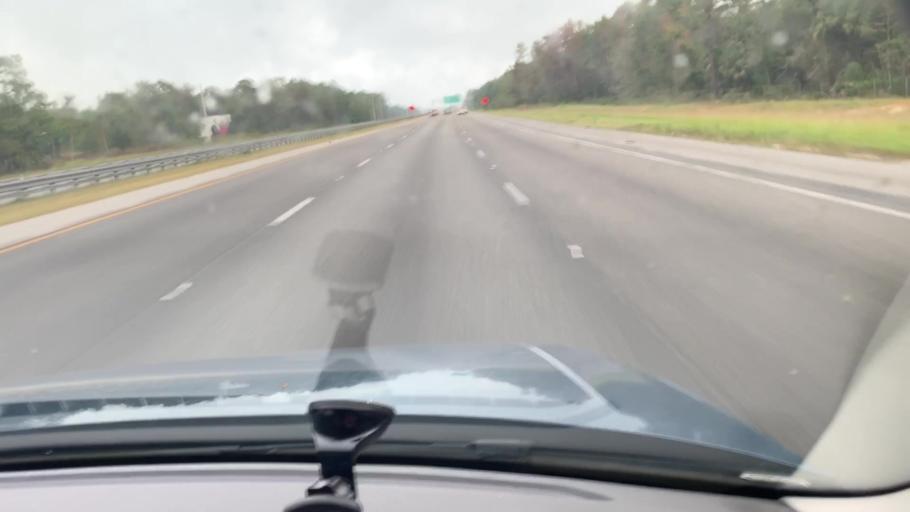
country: US
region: Florida
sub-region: Volusia County
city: South Daytona
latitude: 29.1353
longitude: -81.0640
